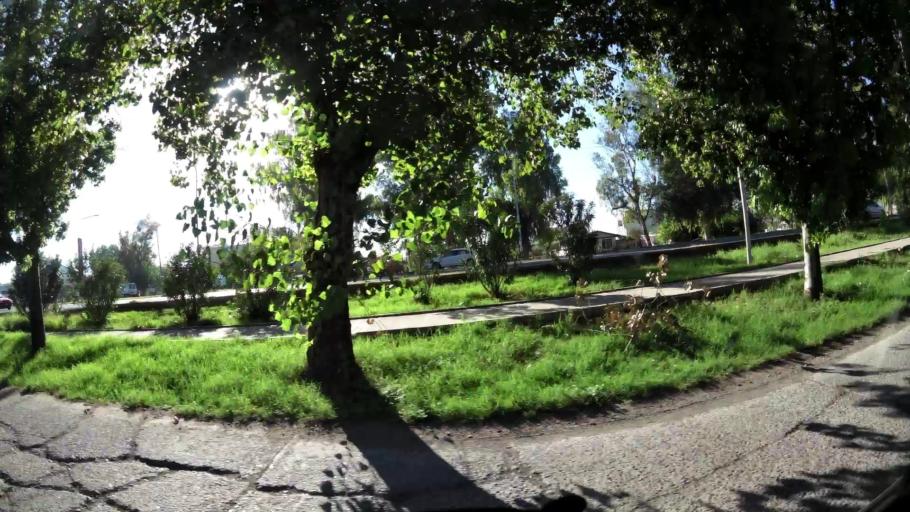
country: AR
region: Mendoza
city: Las Heras
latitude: -32.8564
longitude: -68.8073
